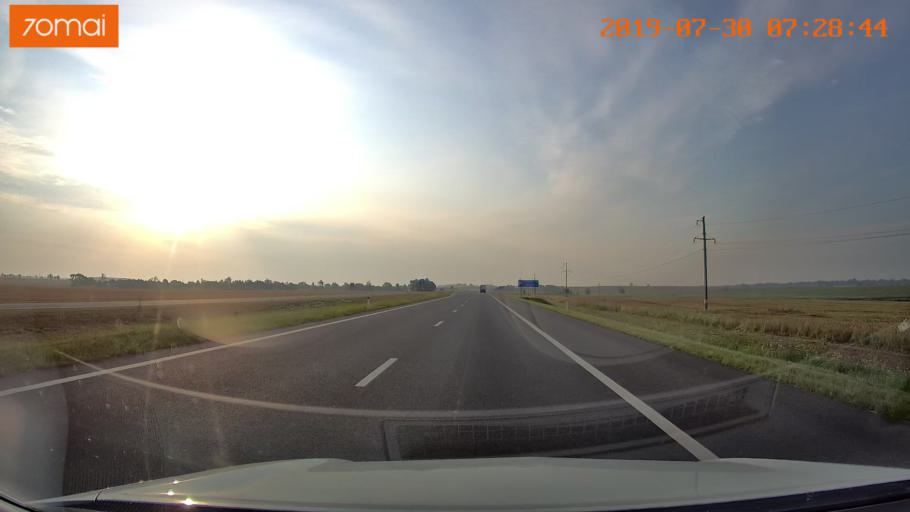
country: RU
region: Kaliningrad
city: Gvardeysk
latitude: 54.6758
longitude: 20.9208
